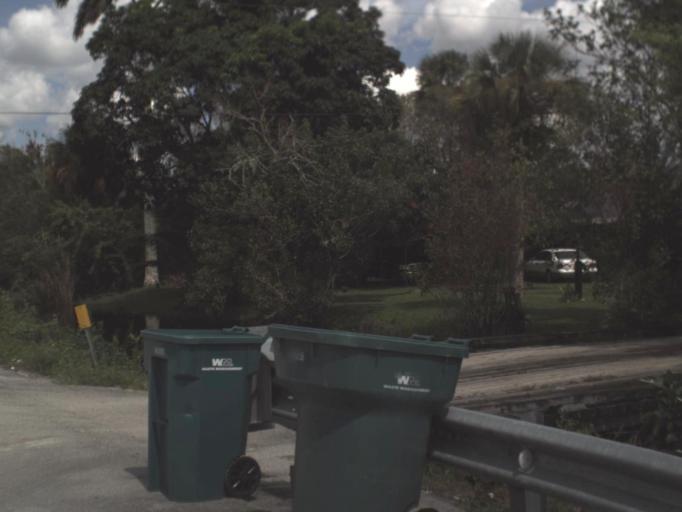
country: US
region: Florida
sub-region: Collier County
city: Lely Resort
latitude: 25.9411
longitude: -81.3574
